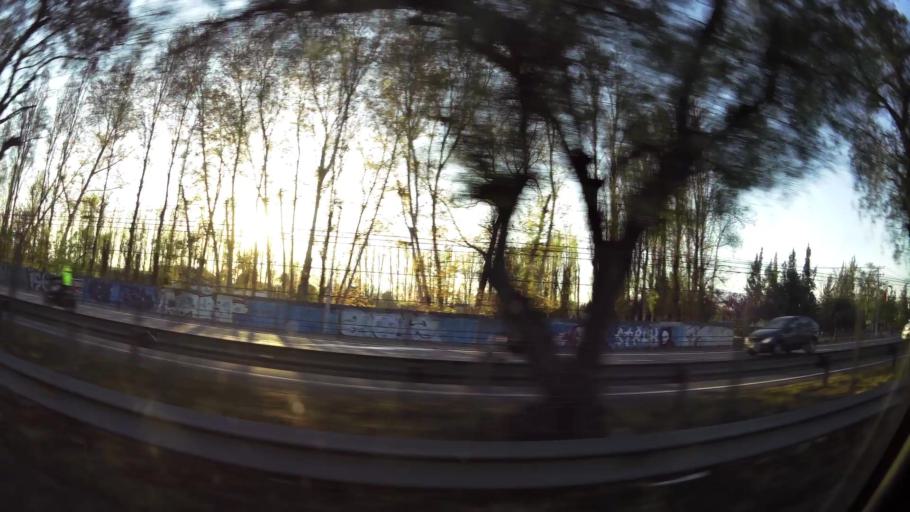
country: CL
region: Santiago Metropolitan
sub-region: Provincia de Talagante
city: Penaflor
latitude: -33.6034
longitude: -70.8484
